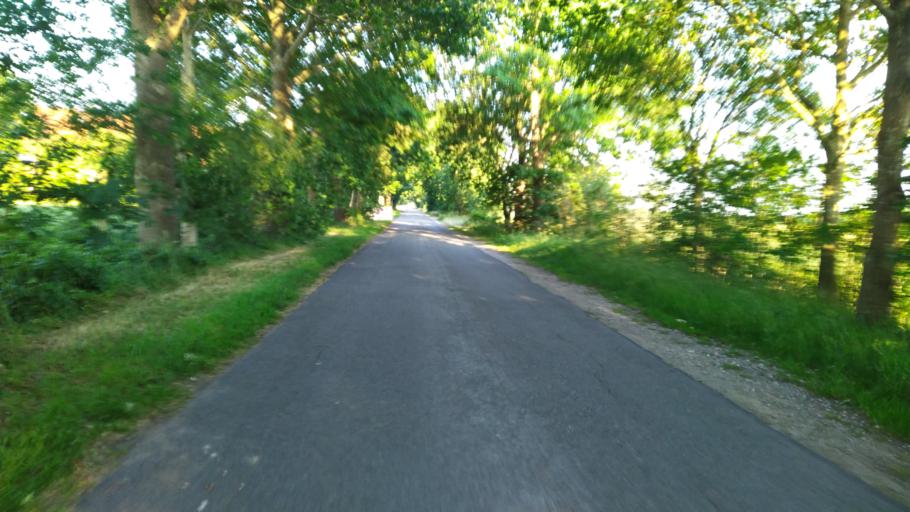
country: DE
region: Lower Saxony
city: Alfstedt
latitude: 53.5545
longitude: 9.0478
